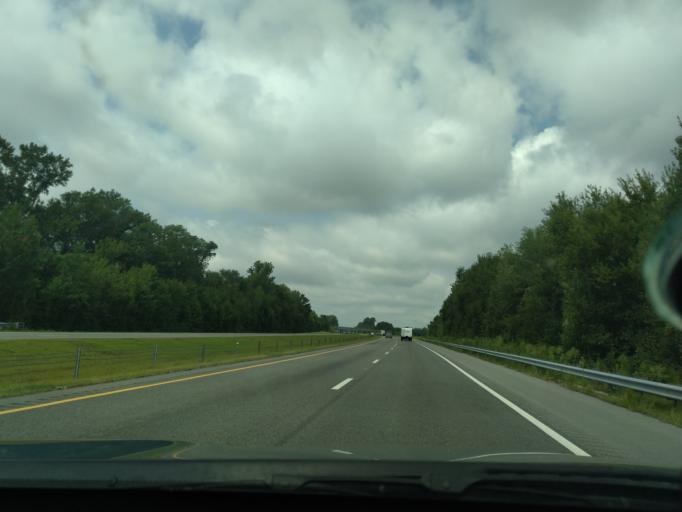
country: US
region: North Carolina
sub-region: Martin County
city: Robersonville
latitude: 35.8335
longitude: -77.3103
